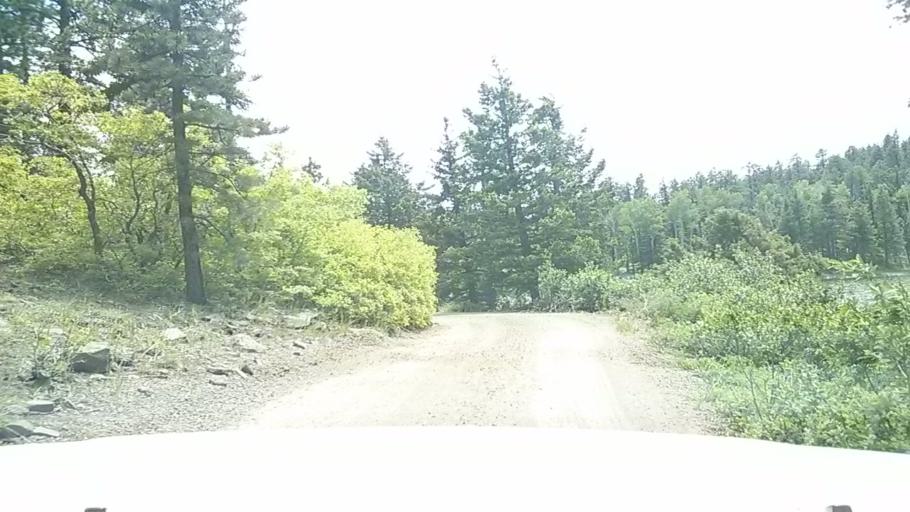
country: US
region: Utah
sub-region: Wayne County
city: Loa
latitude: 37.9375
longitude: -111.6947
